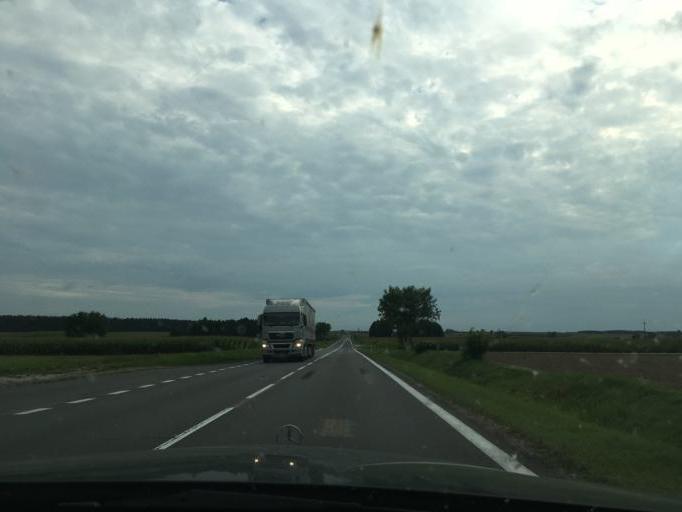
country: PL
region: Podlasie
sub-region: Powiat kolnenski
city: Stawiski
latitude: 53.4215
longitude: 22.1668
